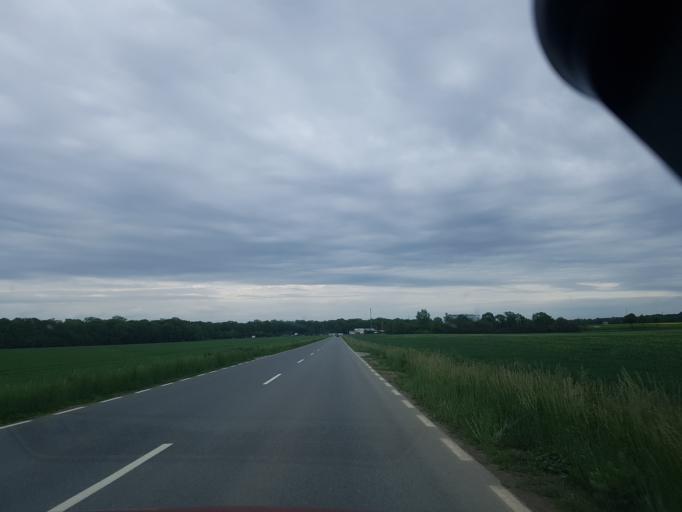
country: PL
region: Lower Silesian Voivodeship
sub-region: Powiat wroclawski
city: Gniechowice
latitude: 50.9842
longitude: 16.8134
